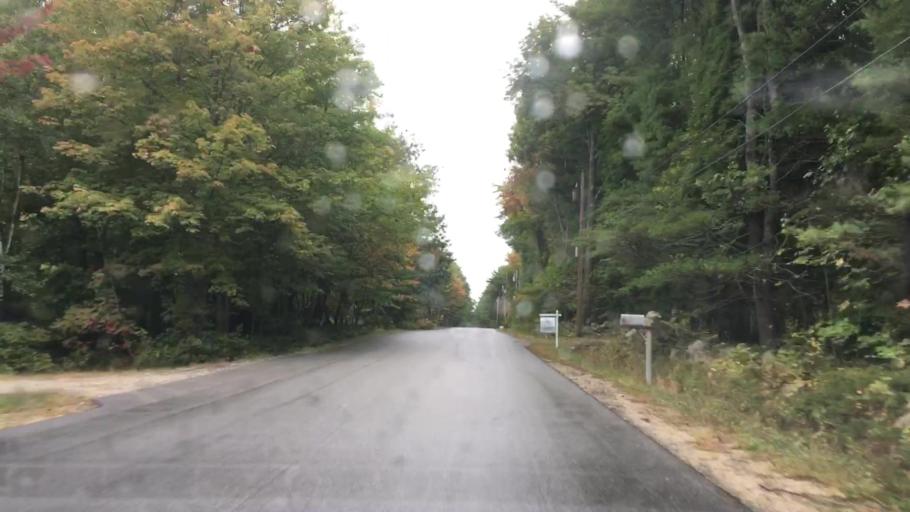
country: US
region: Maine
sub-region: Cumberland County
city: Harrison
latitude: 44.0953
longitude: -70.6582
